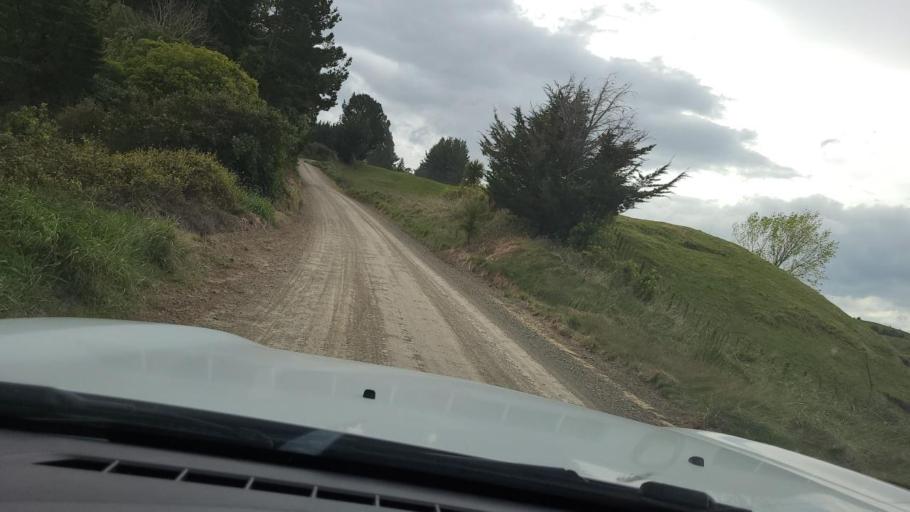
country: NZ
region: Hawke's Bay
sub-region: Napier City
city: Napier
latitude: -39.2619
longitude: 176.8430
